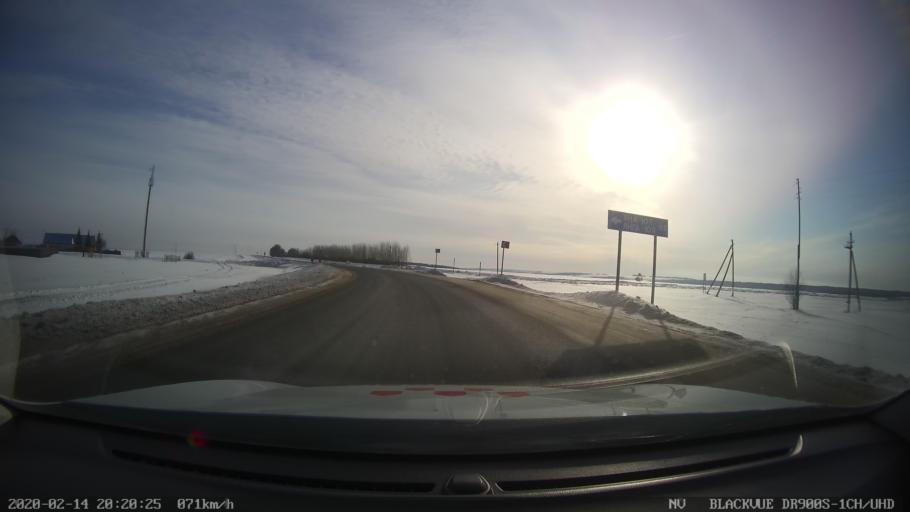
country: RU
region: Tatarstan
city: Verkhniy Uslon
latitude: 55.5574
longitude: 48.9058
